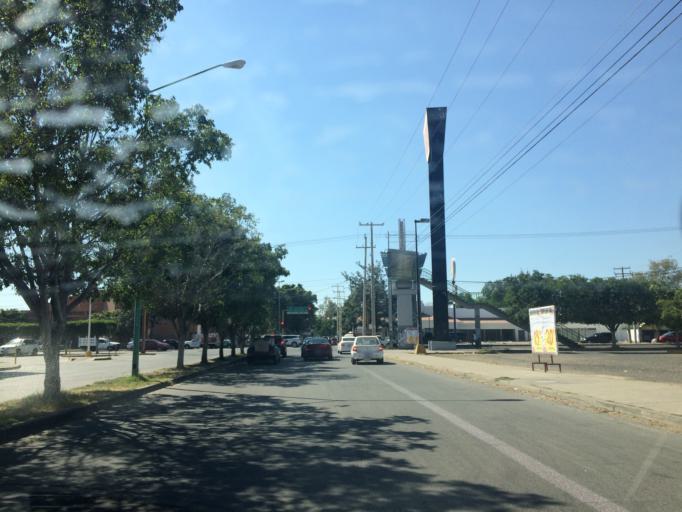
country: MX
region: Guanajuato
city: Leon
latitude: 21.1004
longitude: -101.6706
